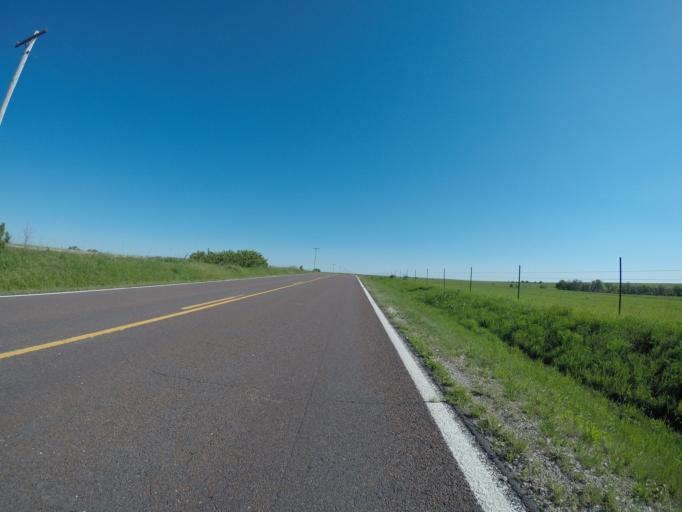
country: US
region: Kansas
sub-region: Osage County
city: Osage City
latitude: 38.6739
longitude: -96.0974
